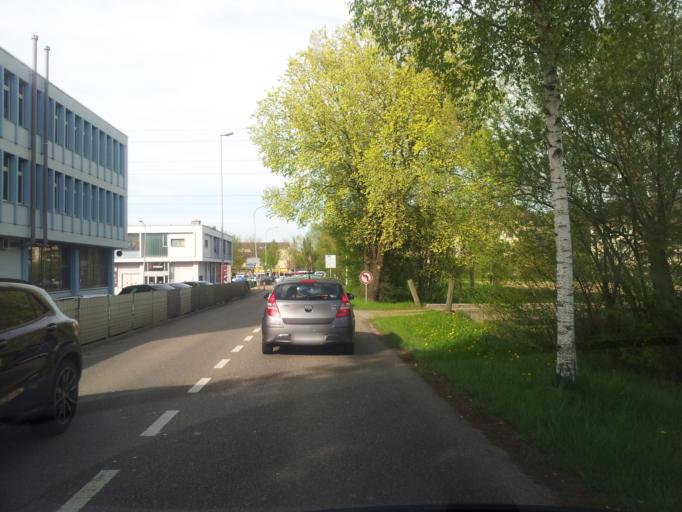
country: CH
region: Zurich
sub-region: Bezirk Uster
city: Duebendorf / Wasserfurren
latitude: 47.3941
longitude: 8.6027
